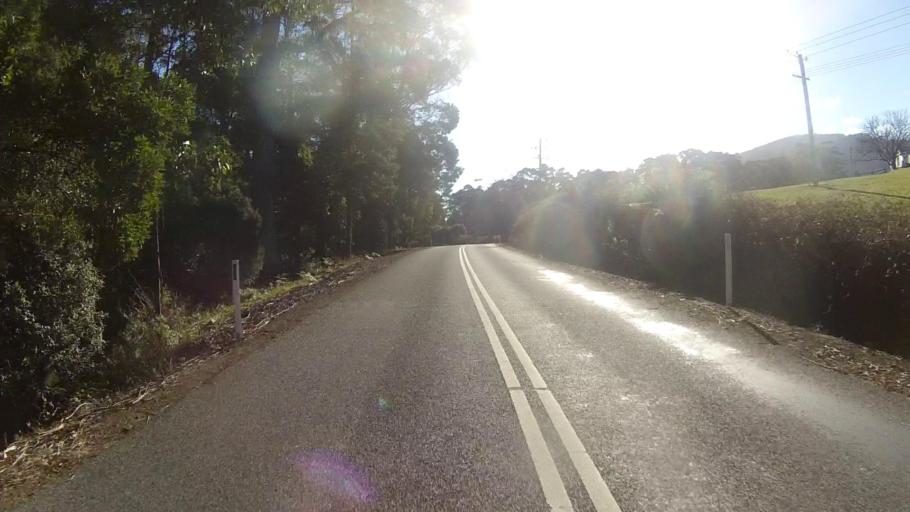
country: AU
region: Tasmania
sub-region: Sorell
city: Sorell
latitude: -42.9951
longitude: 147.9280
